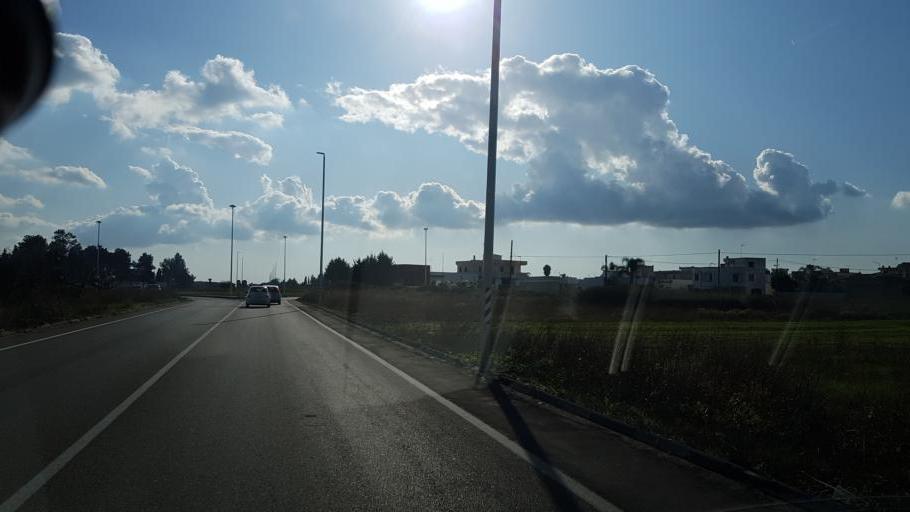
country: IT
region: Apulia
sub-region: Provincia di Lecce
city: Salice Salentino
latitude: 40.3819
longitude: 17.9701
